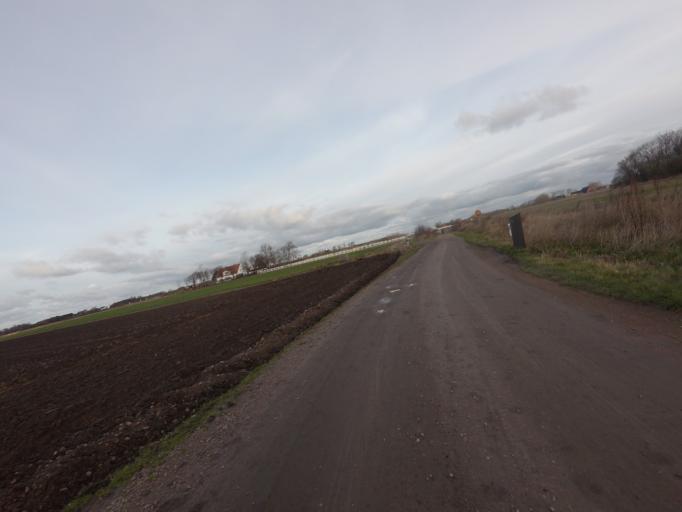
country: SE
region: Skane
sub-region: Hoganas Kommun
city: Hoganas
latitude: 56.1630
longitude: 12.5788
